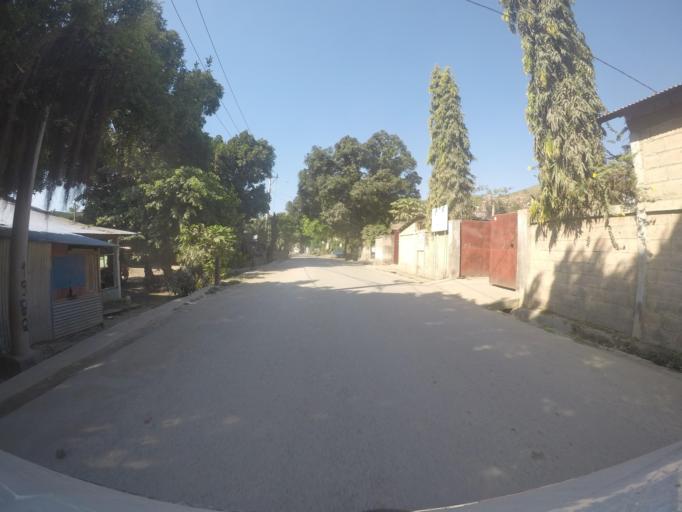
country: TL
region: Dili
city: Dili
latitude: -8.5751
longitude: 125.5414
